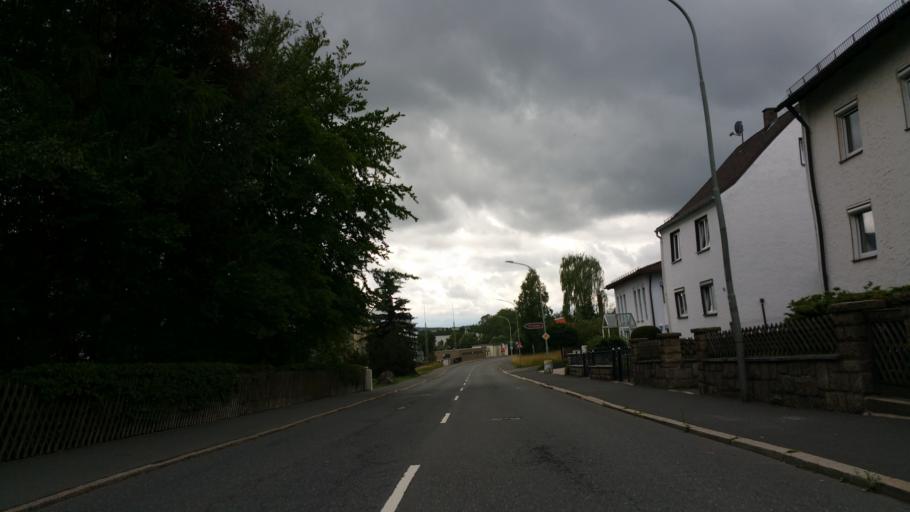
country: DE
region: Bavaria
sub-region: Upper Franconia
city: Rehau
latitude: 50.2566
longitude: 12.0403
